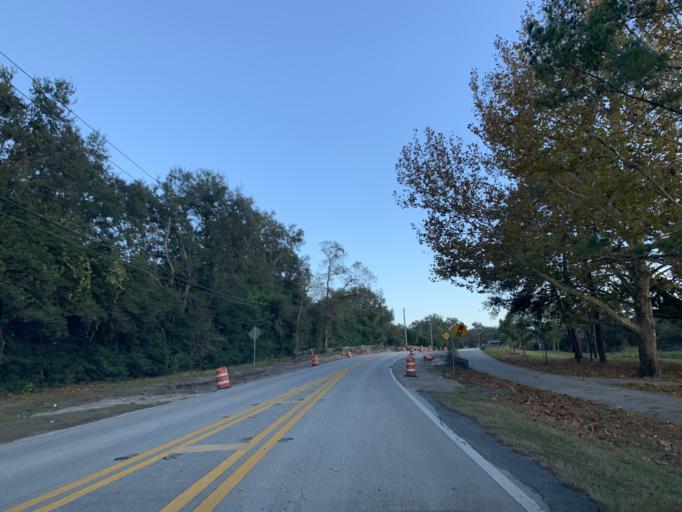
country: US
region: Florida
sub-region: Pinellas County
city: Safety Harbor
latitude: 27.9791
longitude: -82.7397
